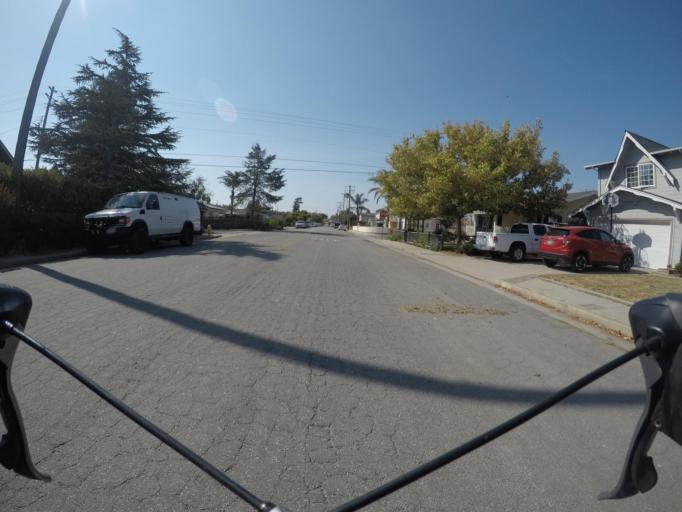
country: US
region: California
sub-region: Santa Cruz County
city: Twin Lakes
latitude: 36.9834
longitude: -122.0034
